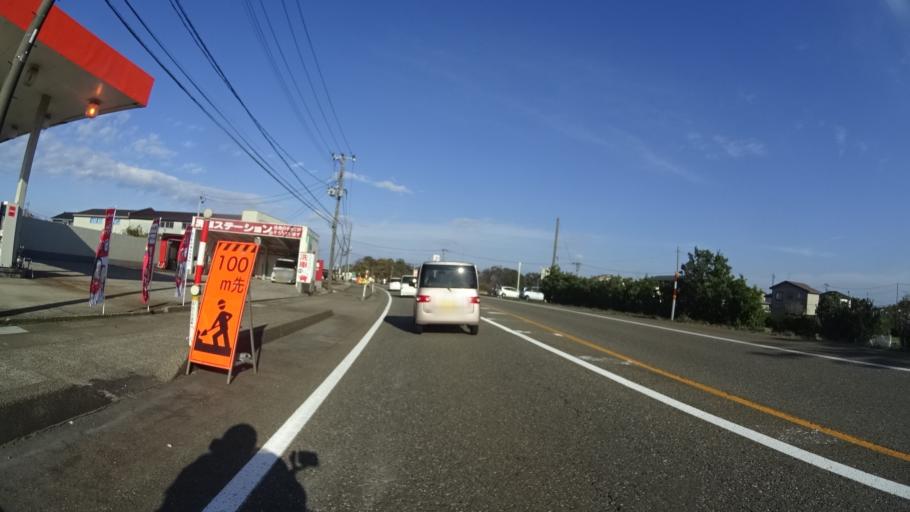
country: JP
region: Niigata
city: Joetsu
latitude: 37.2037
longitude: 138.2980
